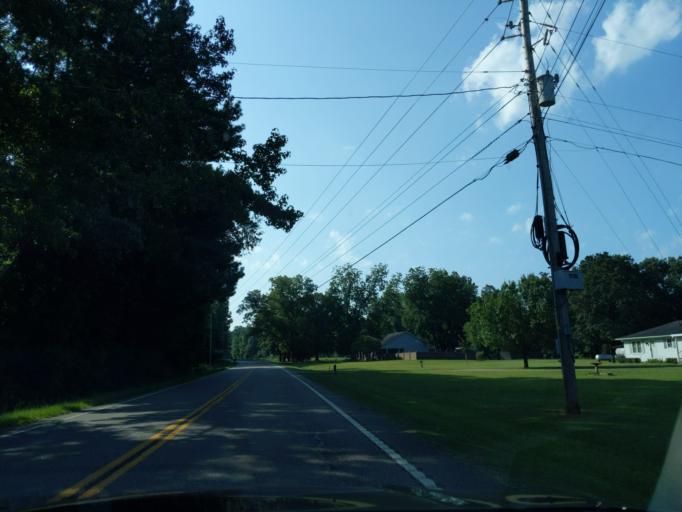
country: US
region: South Carolina
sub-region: Lexington County
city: Leesville
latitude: 34.0472
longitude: -81.5501
